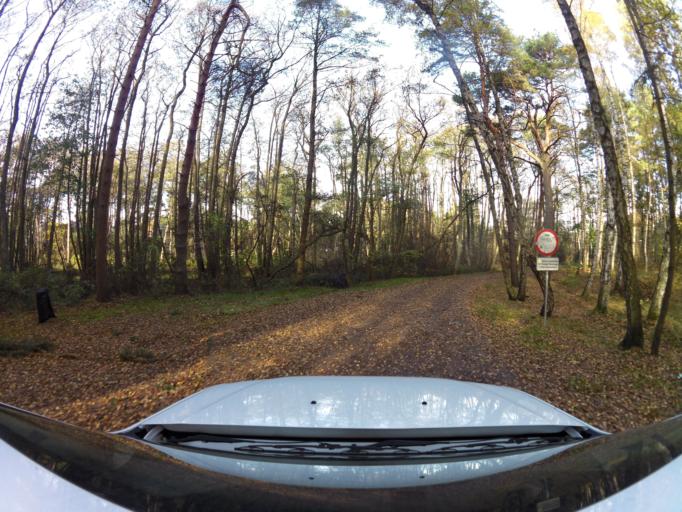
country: PL
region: West Pomeranian Voivodeship
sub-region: Powiat gryficki
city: Karnice
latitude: 54.0979
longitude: 15.0980
